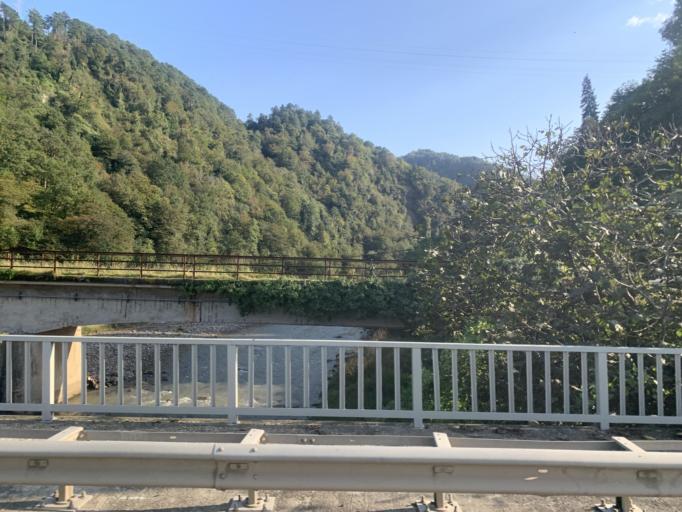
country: TR
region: Trabzon
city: Of
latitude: 40.9295
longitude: 40.2345
